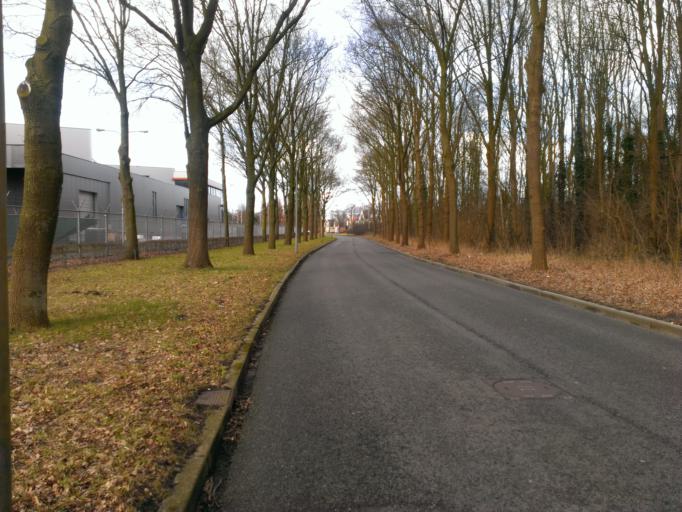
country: NL
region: Overijssel
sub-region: Gemeente Almelo
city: Almelo
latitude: 52.3386
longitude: 6.6939
